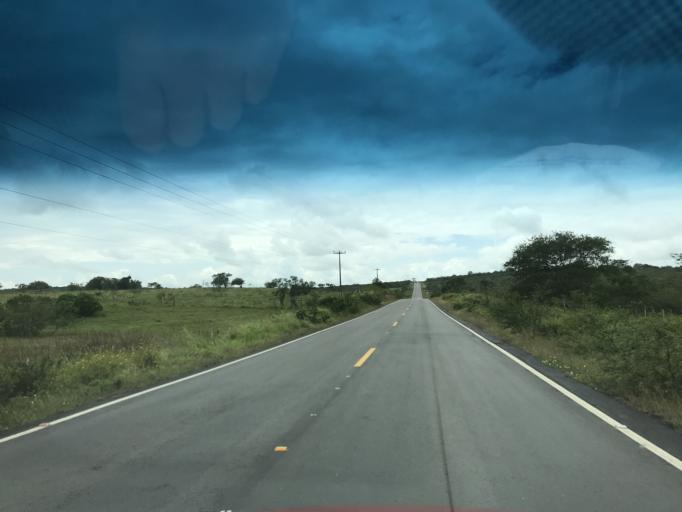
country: BR
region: Bahia
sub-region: Conceicao Do Almeida
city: Conceicao do Almeida
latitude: -12.6715
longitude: -39.2907
